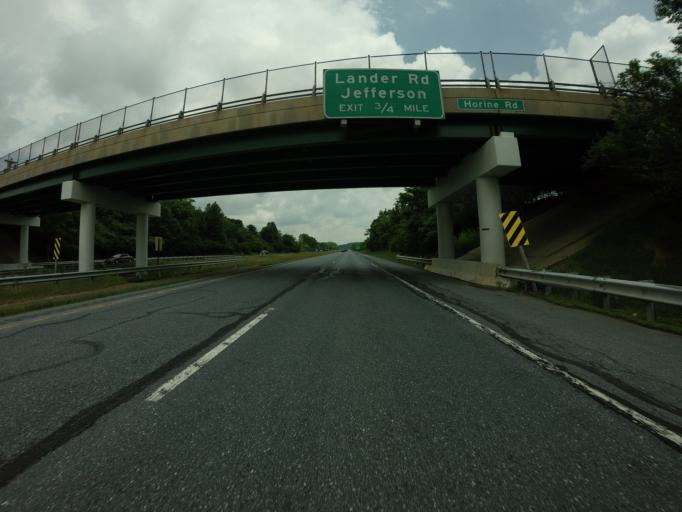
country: US
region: Maryland
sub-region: Frederick County
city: Jefferson
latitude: 39.3577
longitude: -77.5493
